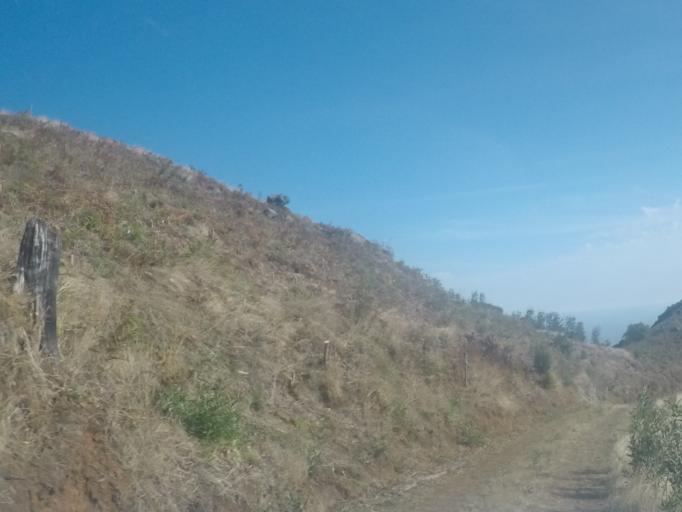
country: PT
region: Madeira
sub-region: Funchal
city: Nossa Senhora do Monte
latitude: 32.6963
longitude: -16.9124
